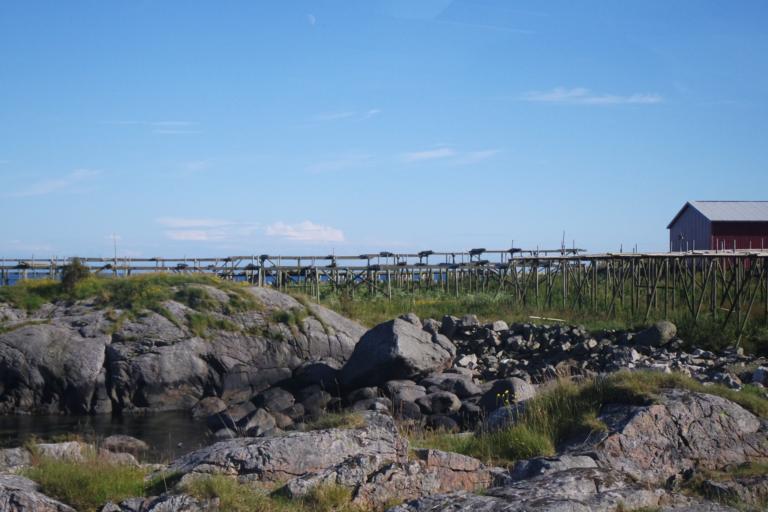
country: NO
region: Nordland
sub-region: Moskenes
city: Reine
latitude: 67.9431
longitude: 13.1205
